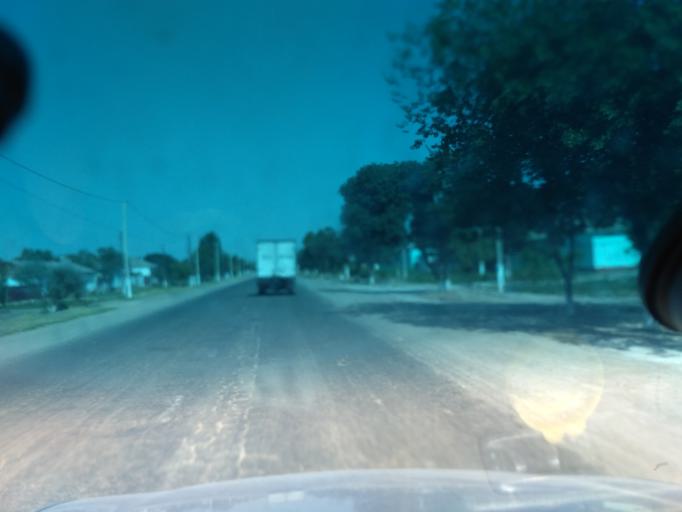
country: UZ
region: Sirdaryo
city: Guliston
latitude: 40.4874
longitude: 68.8826
